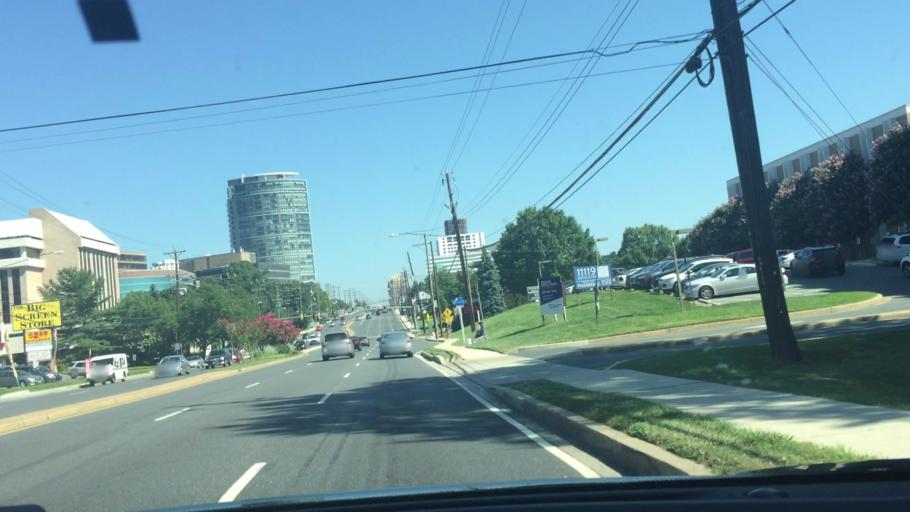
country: US
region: Maryland
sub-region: Montgomery County
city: North Bethesda
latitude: 39.0388
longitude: -77.1087
